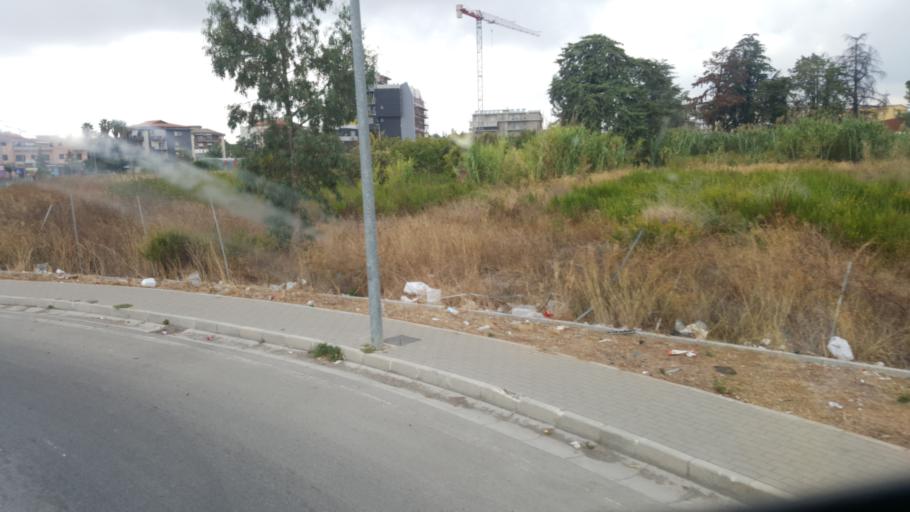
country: IT
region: Campania
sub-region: Provincia di Salerno
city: Battipaglia
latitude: 40.6026
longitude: 14.9840
